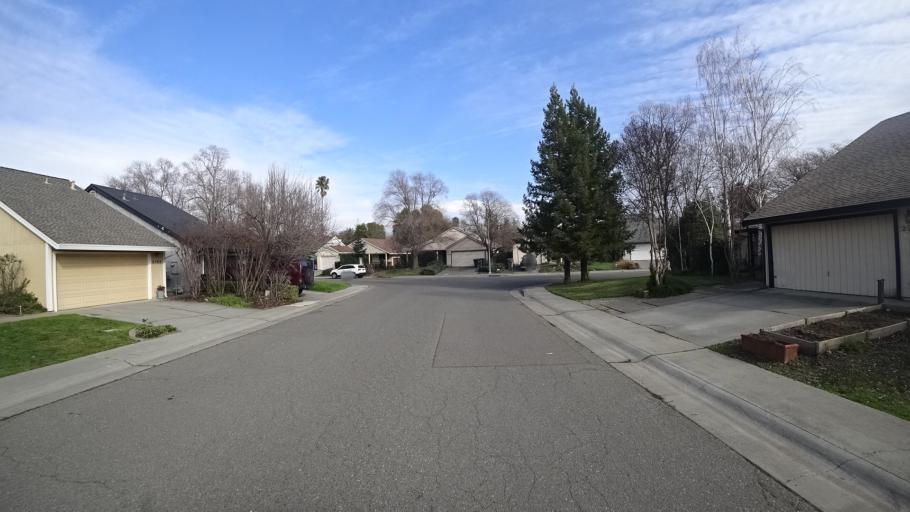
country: US
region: California
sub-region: Yolo County
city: Davis
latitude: 38.5452
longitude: -121.7181
